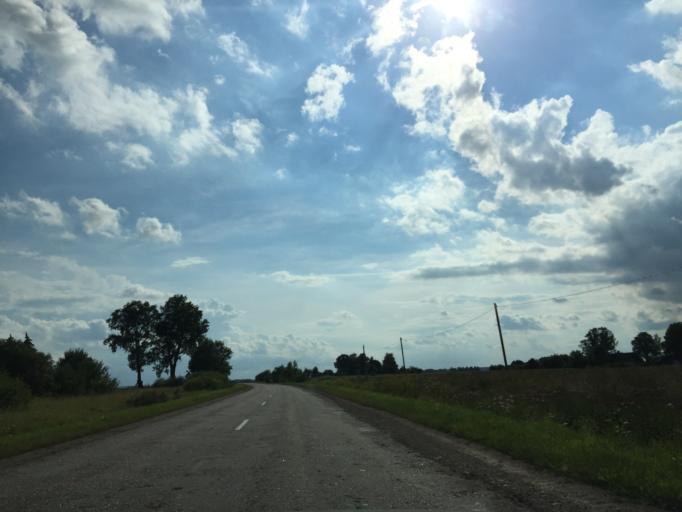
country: LV
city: Tervete
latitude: 56.5825
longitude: 23.4469
